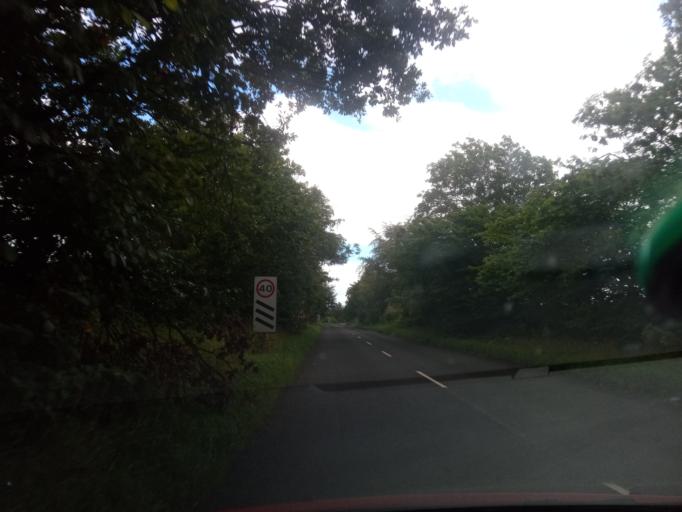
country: GB
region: Scotland
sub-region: The Scottish Borders
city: Kelso
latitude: 55.6084
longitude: -2.3975
